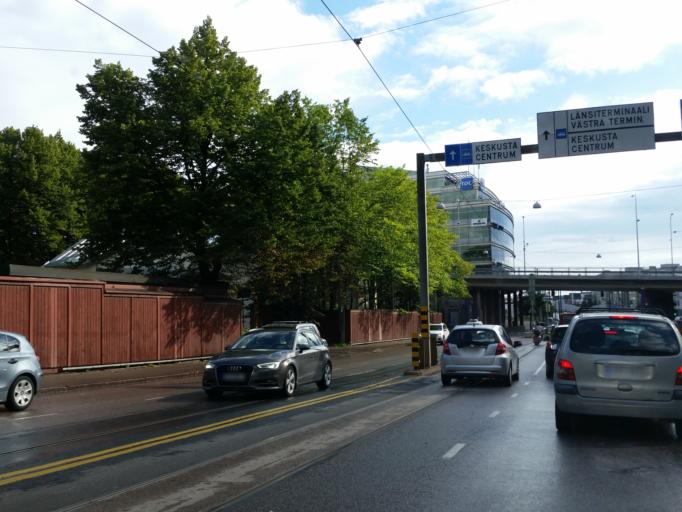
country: FI
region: Uusimaa
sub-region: Helsinki
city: Helsinki
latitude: 60.1656
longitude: 24.9211
